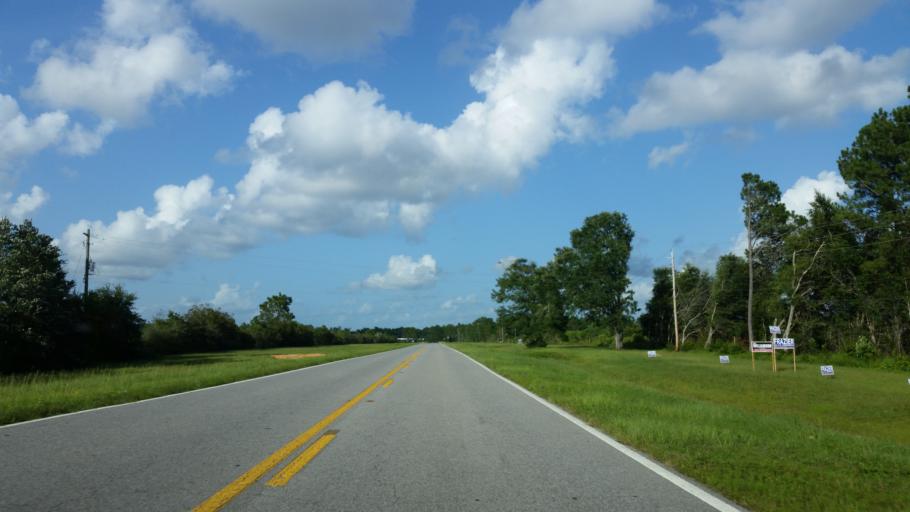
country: US
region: Florida
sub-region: Santa Rosa County
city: Bagdad
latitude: 30.5613
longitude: -87.0396
